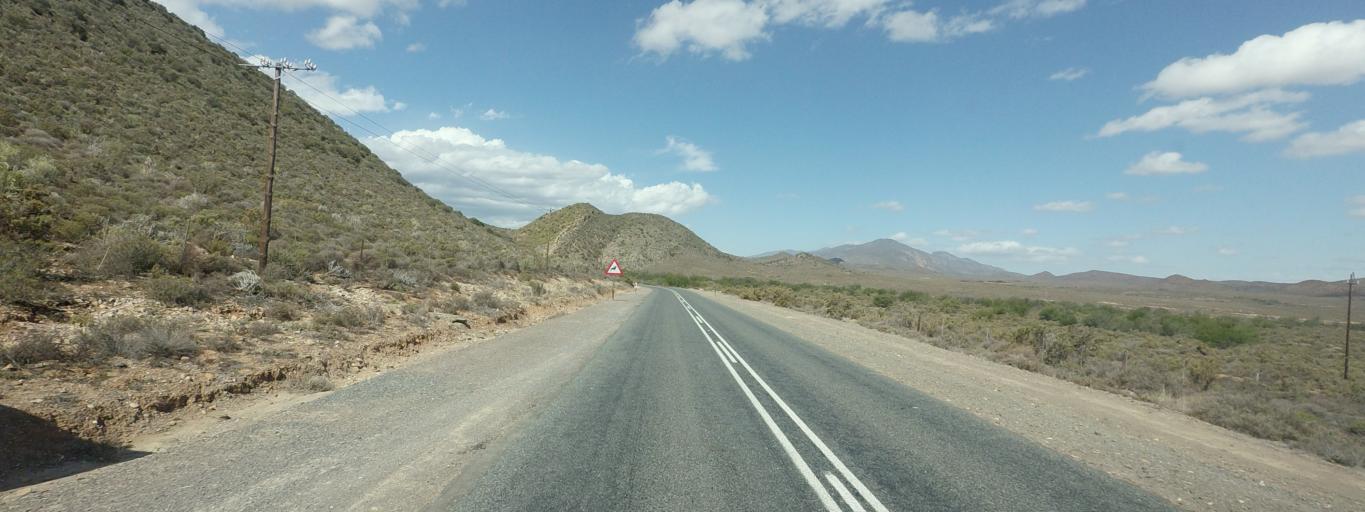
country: ZA
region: Western Cape
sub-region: Eden District Municipality
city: Ladismith
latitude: -33.5888
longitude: 21.1855
